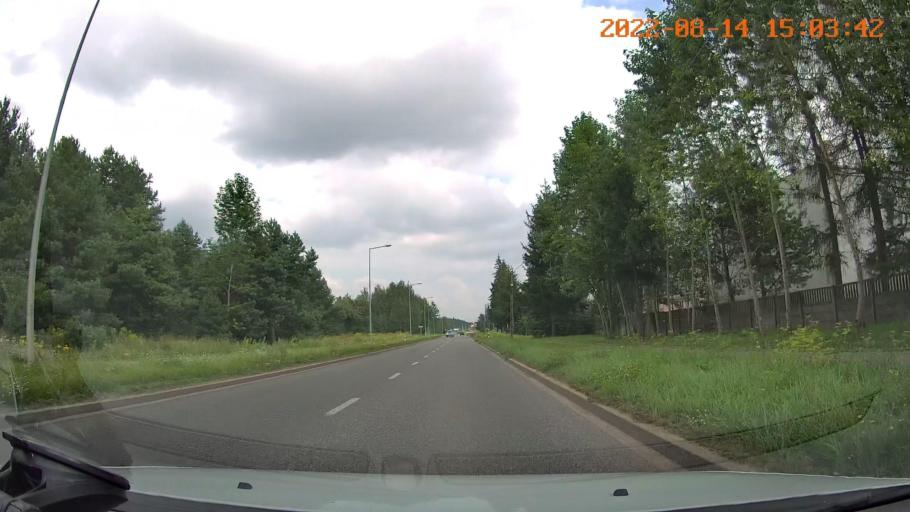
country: PL
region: Swietokrzyskie
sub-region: Powiat kielecki
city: Kostomloty Drugie
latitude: 50.8822
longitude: 20.5383
